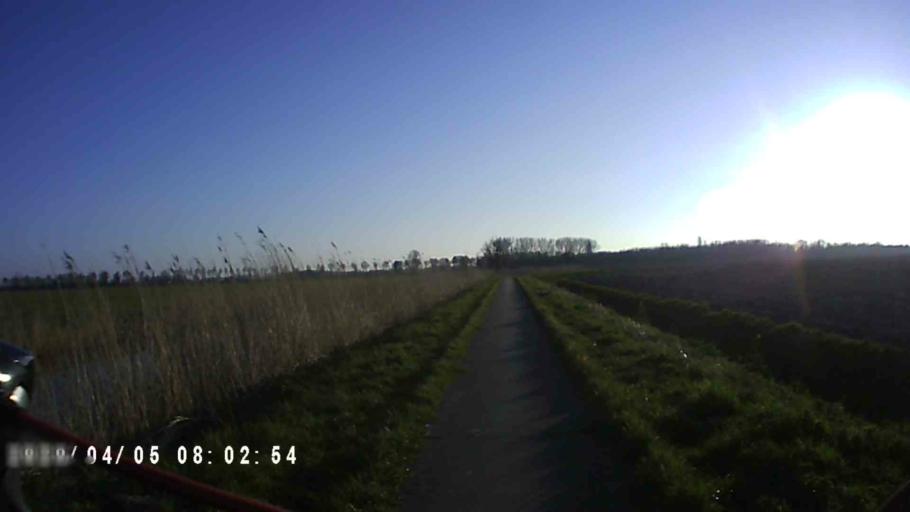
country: NL
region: Groningen
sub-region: Gemeente Zuidhorn
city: Oldehove
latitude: 53.3480
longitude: 6.4352
